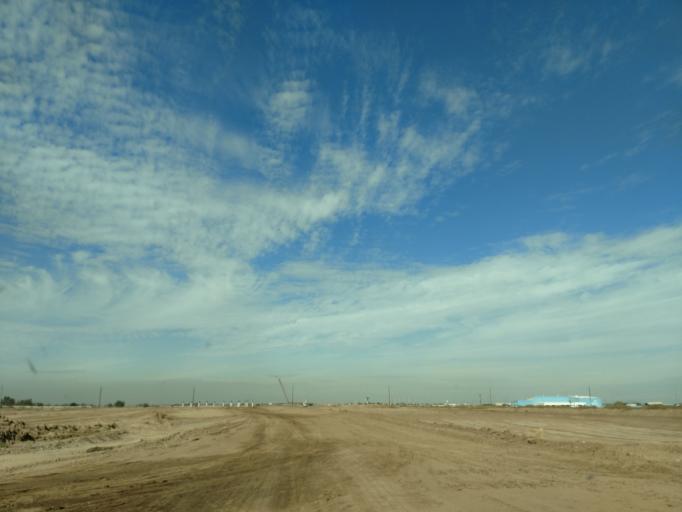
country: US
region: Arizona
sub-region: Maricopa County
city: Laveen
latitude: 33.3879
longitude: -112.1909
